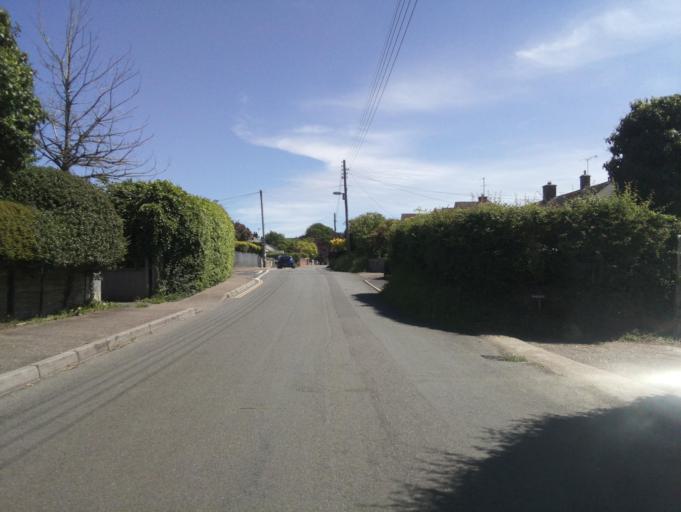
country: GB
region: England
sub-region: Devon
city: Ottery St Mary
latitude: 50.7500
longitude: -3.2728
